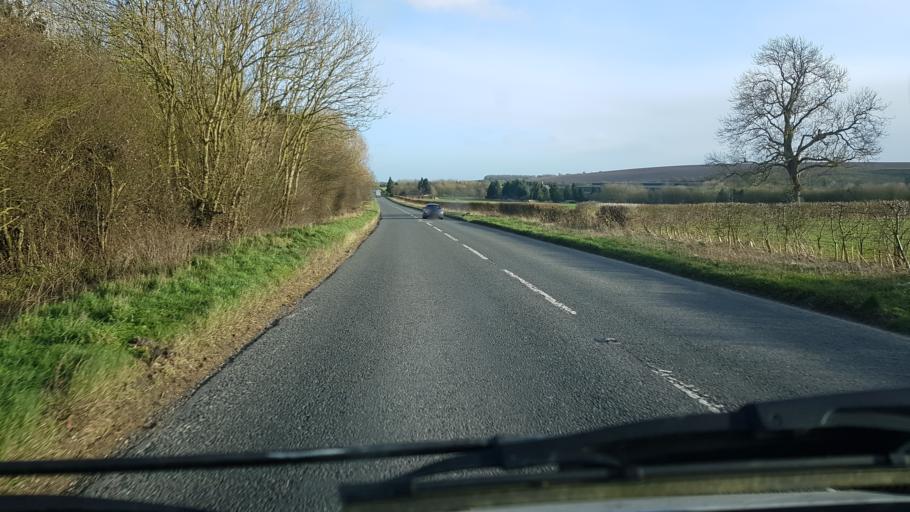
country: GB
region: England
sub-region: Wiltshire
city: Burbage
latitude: 51.3265
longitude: -1.6776
